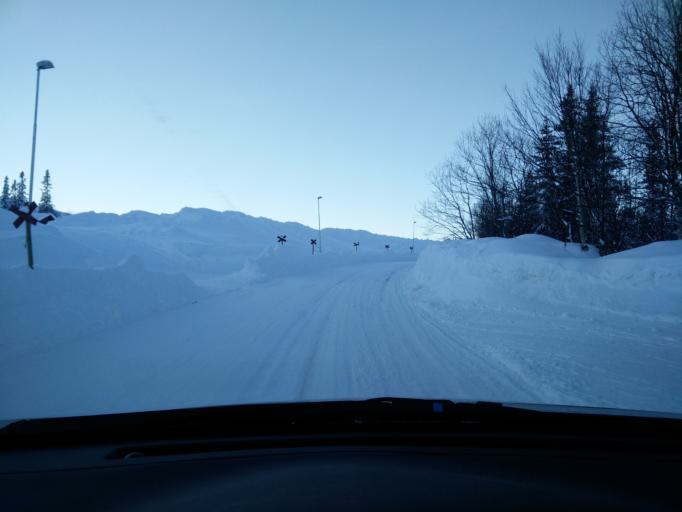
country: SE
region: Jaemtland
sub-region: Bergs Kommun
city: Hoverberg
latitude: 62.5028
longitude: 14.1001
